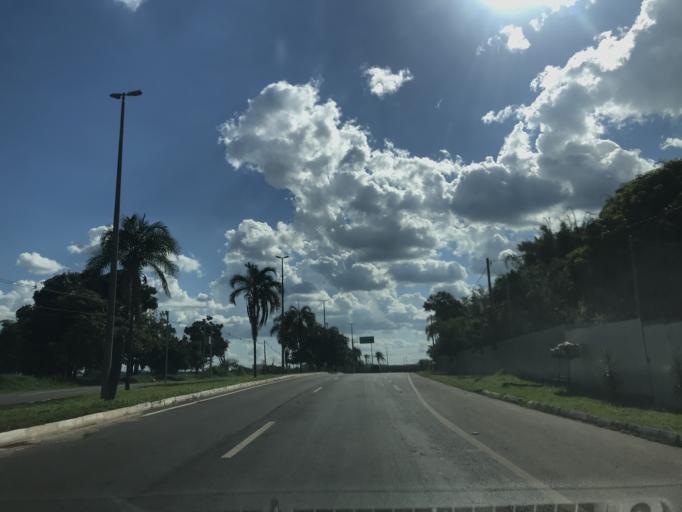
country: BR
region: Federal District
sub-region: Brasilia
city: Brasilia
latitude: -15.7185
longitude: -47.8951
